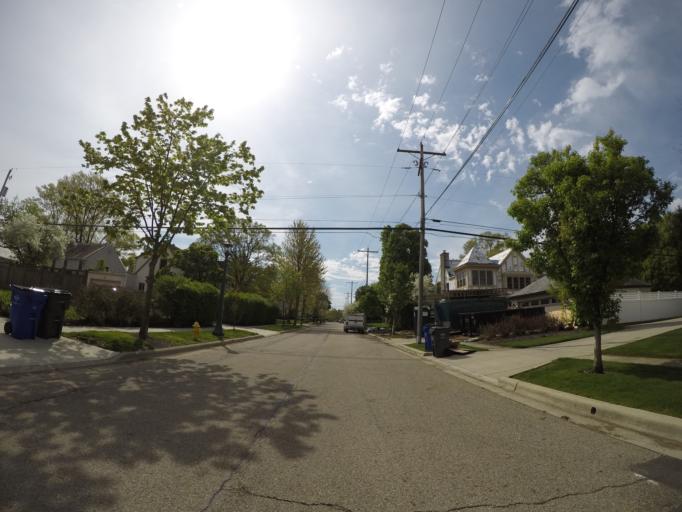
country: US
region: Ohio
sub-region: Franklin County
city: Upper Arlington
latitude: 40.0024
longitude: -83.0594
